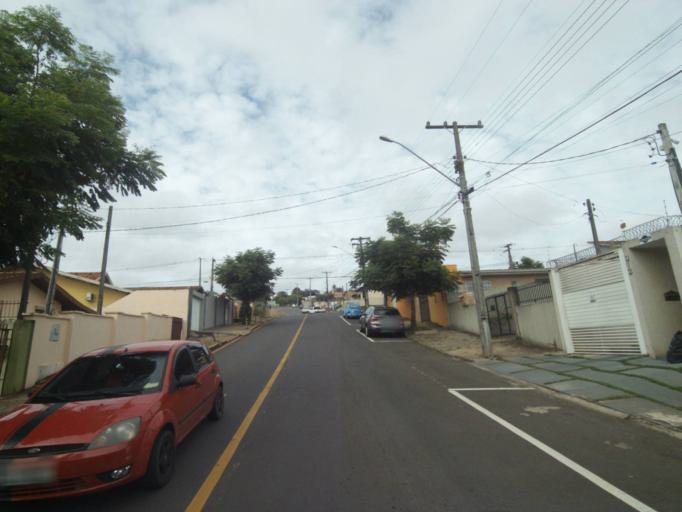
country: BR
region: Parana
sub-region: Telemaco Borba
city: Telemaco Borba
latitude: -24.3371
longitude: -50.6222
